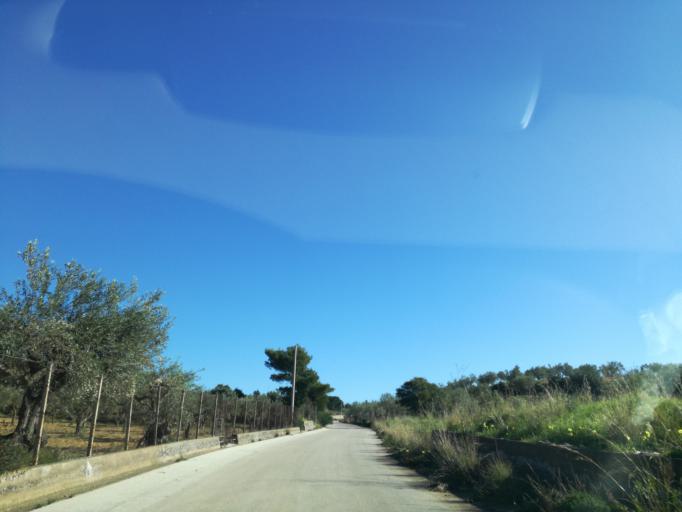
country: IT
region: Sicily
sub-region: Provincia di Caltanissetta
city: Niscemi
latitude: 37.0607
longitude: 14.3493
